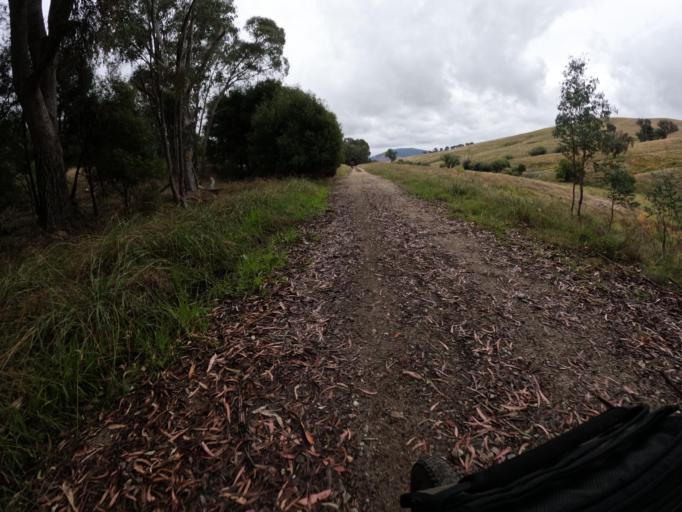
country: AU
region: New South Wales
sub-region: Greater Hume Shire
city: Holbrook
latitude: -36.1603
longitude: 147.4095
